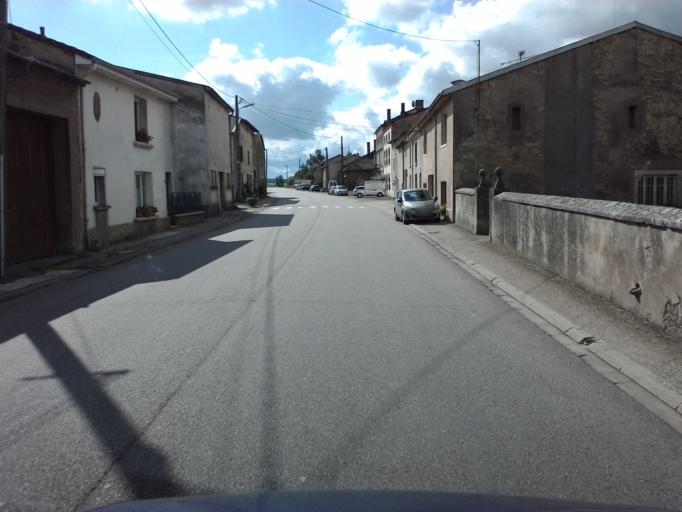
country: FR
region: Lorraine
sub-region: Departement de Meurthe-et-Moselle
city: Colombey-les-Belles
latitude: 48.4839
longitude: 5.8491
